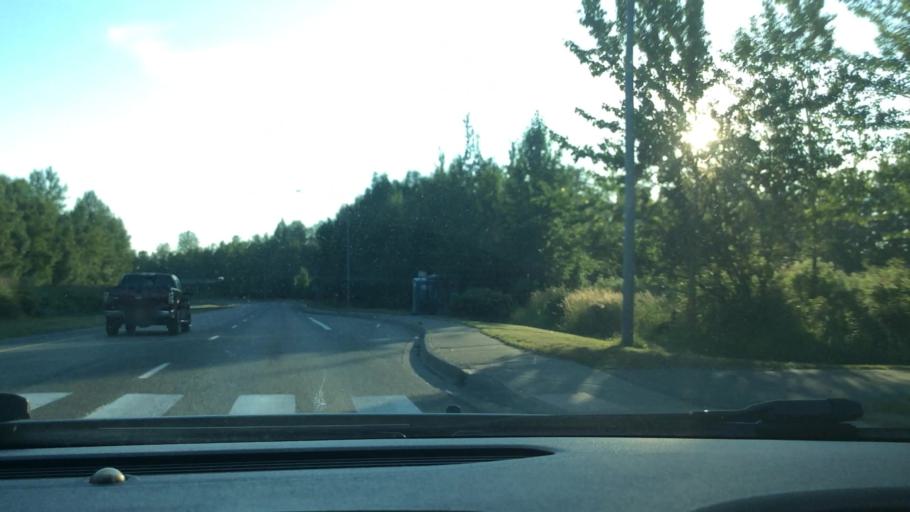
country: US
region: Alaska
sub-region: Anchorage Municipality
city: Anchorage
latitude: 61.1990
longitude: -149.8158
